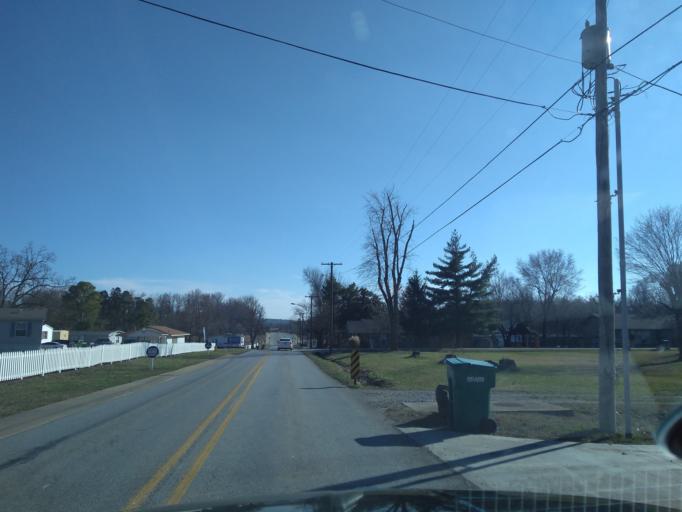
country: US
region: Arkansas
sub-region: Washington County
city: Johnson
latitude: 36.1315
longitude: -94.1630
